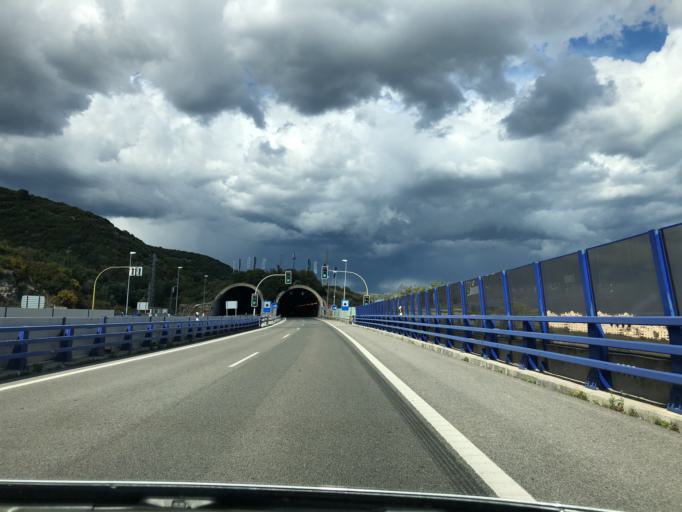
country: ES
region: Andalusia
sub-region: Provincia de Malaga
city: Estepona
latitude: 36.4268
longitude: -5.2042
